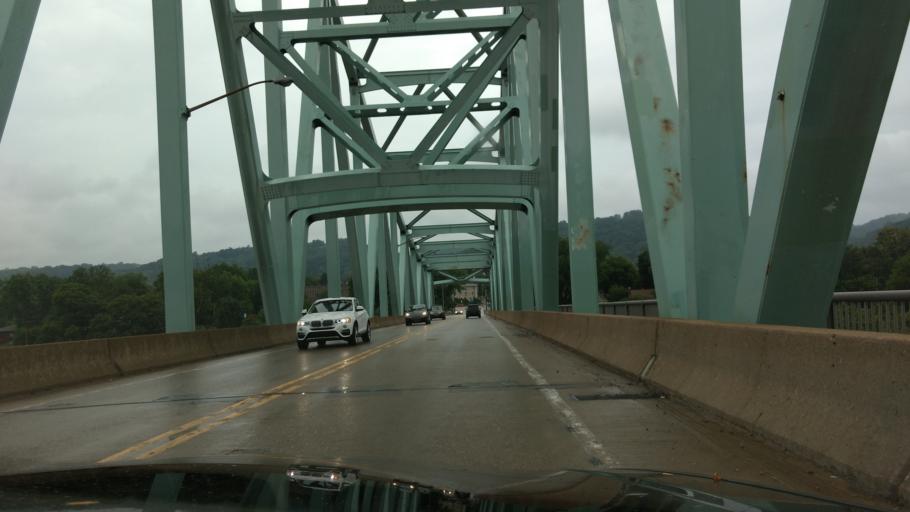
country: US
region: Pennsylvania
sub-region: Allegheny County
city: Sewickley
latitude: 40.5337
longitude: -80.1871
